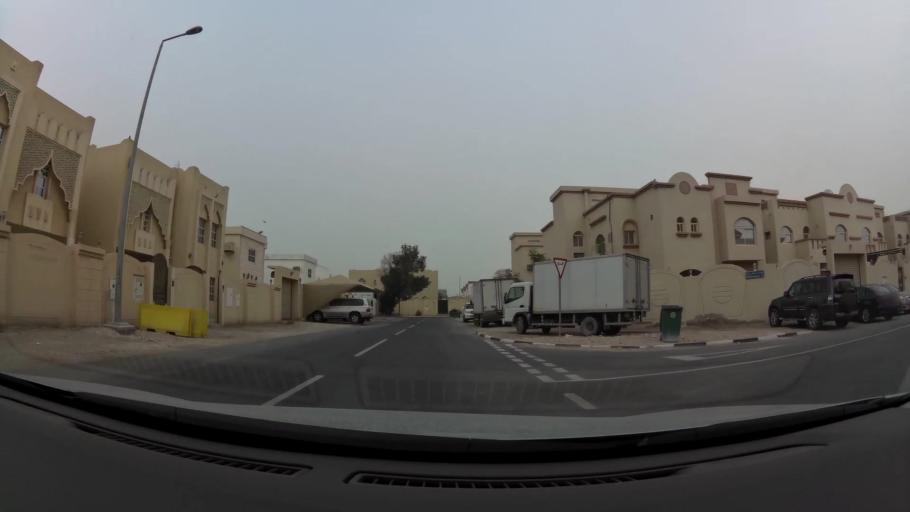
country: QA
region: Baladiyat ad Dawhah
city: Doha
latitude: 25.2544
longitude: 51.4838
